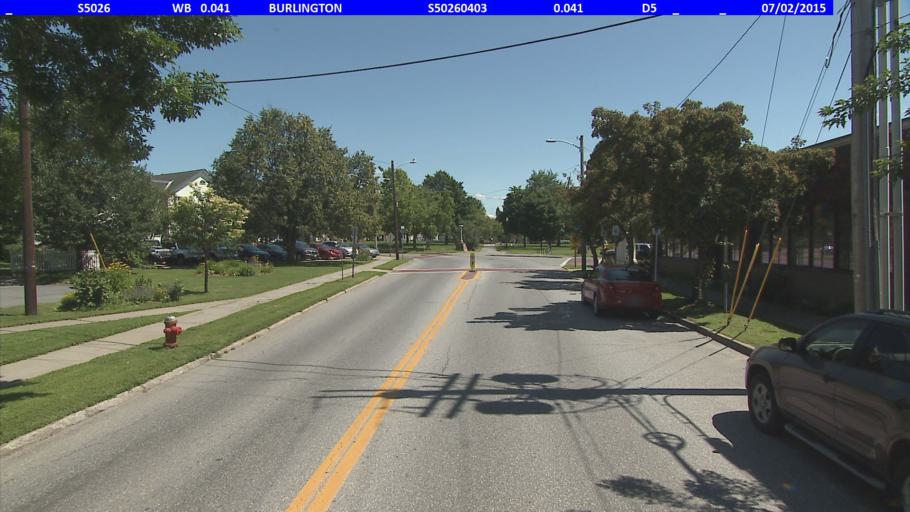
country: US
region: Vermont
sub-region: Chittenden County
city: Burlington
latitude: 44.4825
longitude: -73.2208
